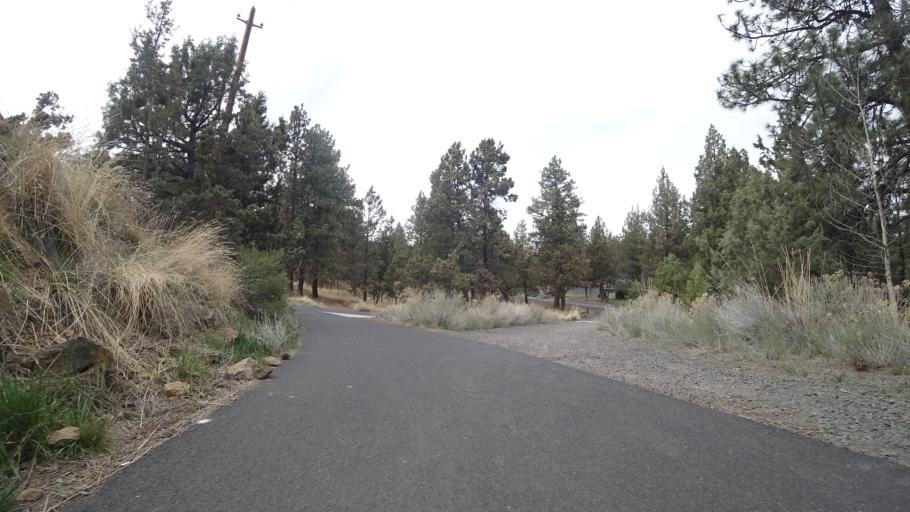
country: US
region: Oregon
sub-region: Deschutes County
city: Bend
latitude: 44.0513
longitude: -121.2904
